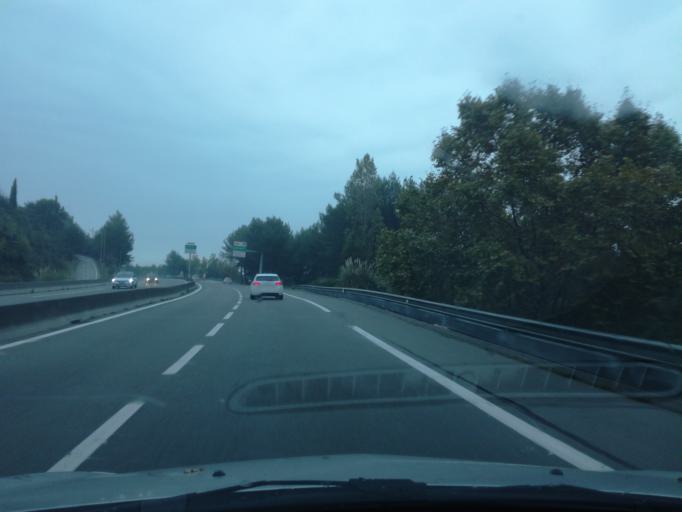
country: FR
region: Provence-Alpes-Cote d'Azur
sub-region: Departement des Alpes-Maritimes
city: Mougins
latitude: 43.5996
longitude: 7.0025
